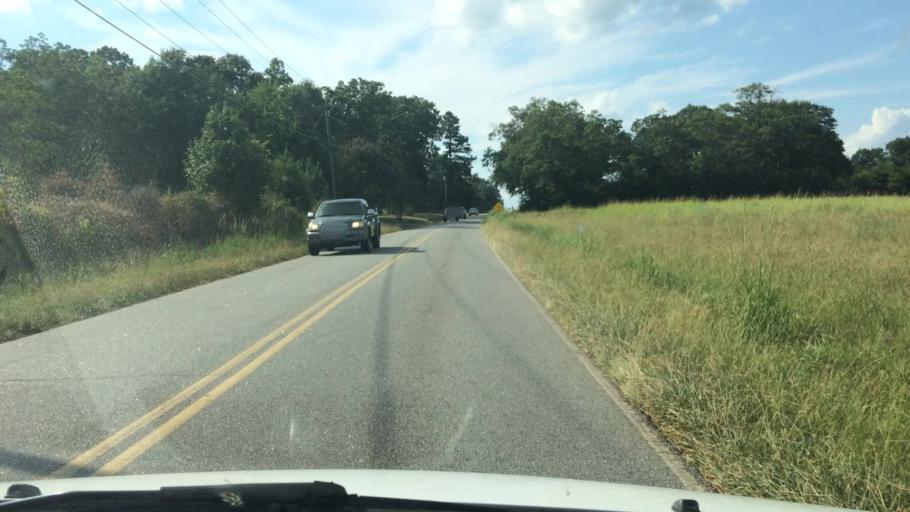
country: US
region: South Carolina
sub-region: Anderson County
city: Anderson
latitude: 34.5639
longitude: -82.6109
